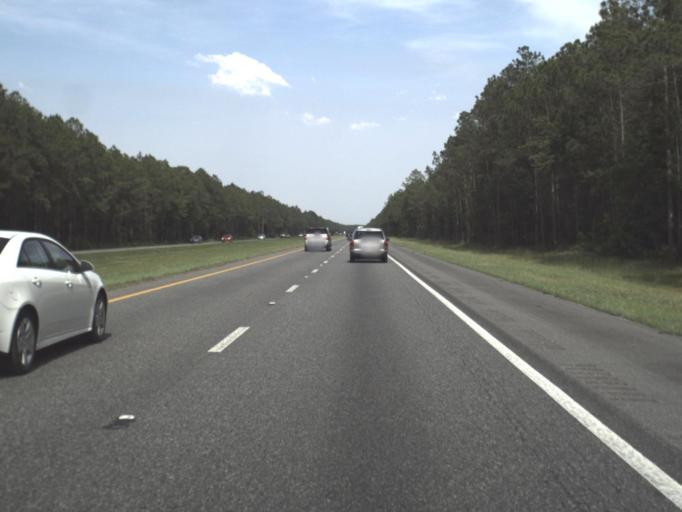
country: US
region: Florida
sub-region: Union County
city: Lake Butler
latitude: 30.2541
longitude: -82.3603
